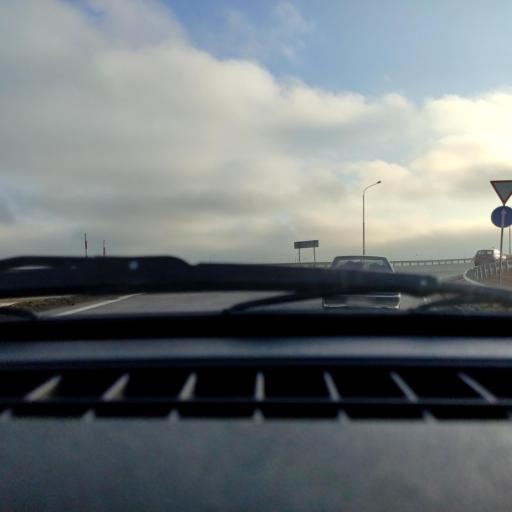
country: RU
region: Bashkortostan
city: Chishmy
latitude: 54.6696
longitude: 55.4014
